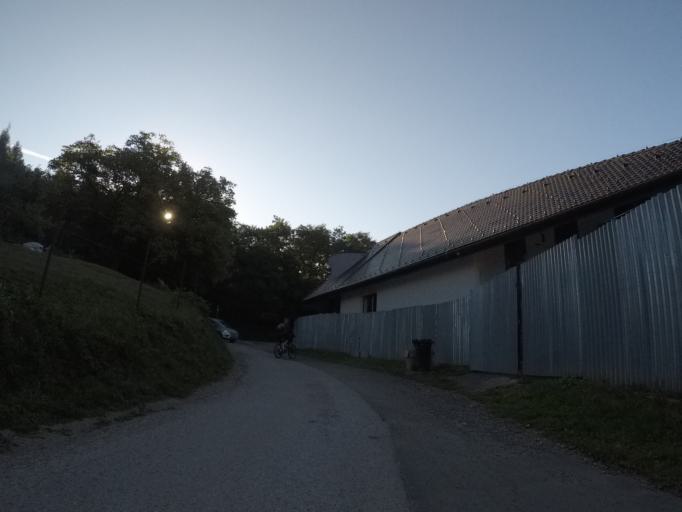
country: SK
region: Kosicky
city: Kosice
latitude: 48.7298
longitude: 21.1433
